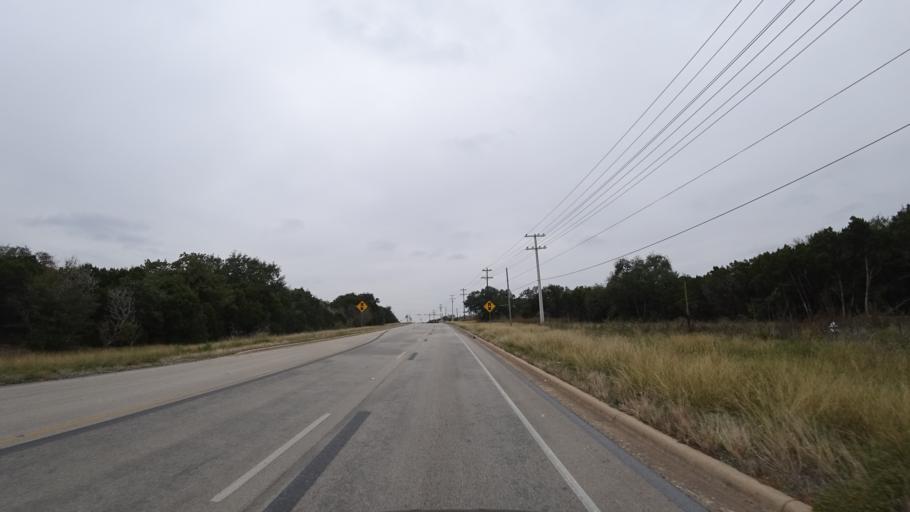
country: US
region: Texas
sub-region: Travis County
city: Shady Hollow
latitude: 30.1808
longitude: -97.8975
